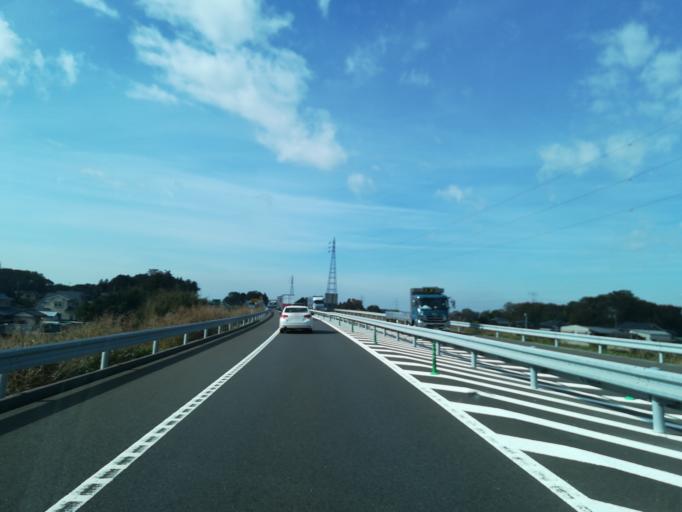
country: JP
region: Ibaraki
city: Sakai
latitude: 36.1277
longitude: 139.7969
